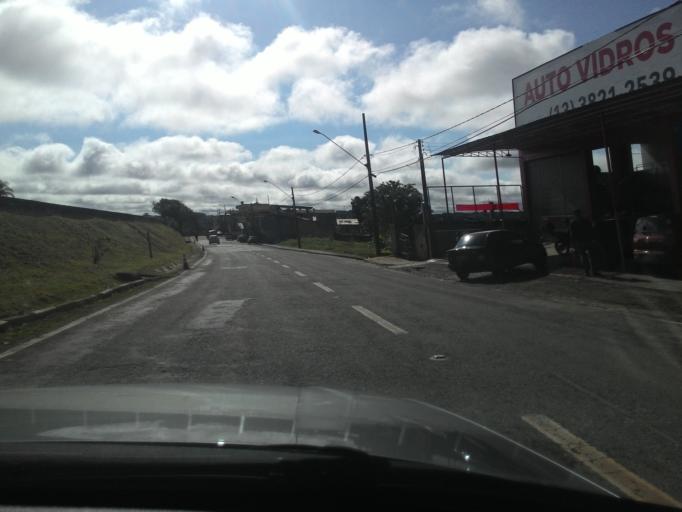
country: BR
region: Sao Paulo
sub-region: Registro
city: Registro
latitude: -24.4933
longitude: -47.8371
